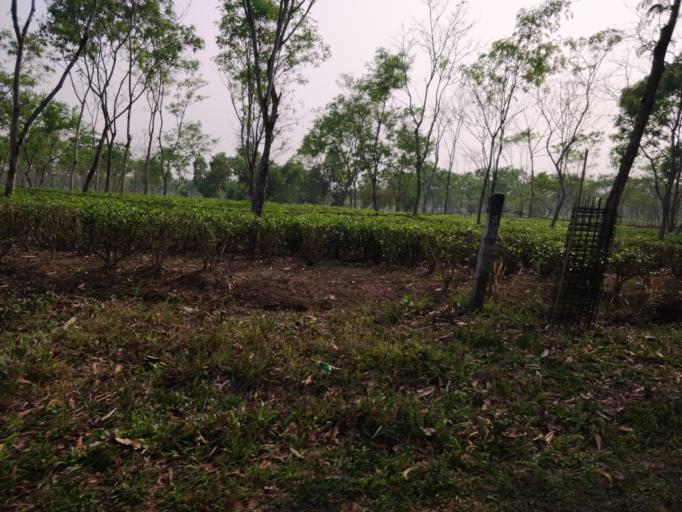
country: IN
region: Tripura
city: Khowai
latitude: 24.1294
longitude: 91.3905
